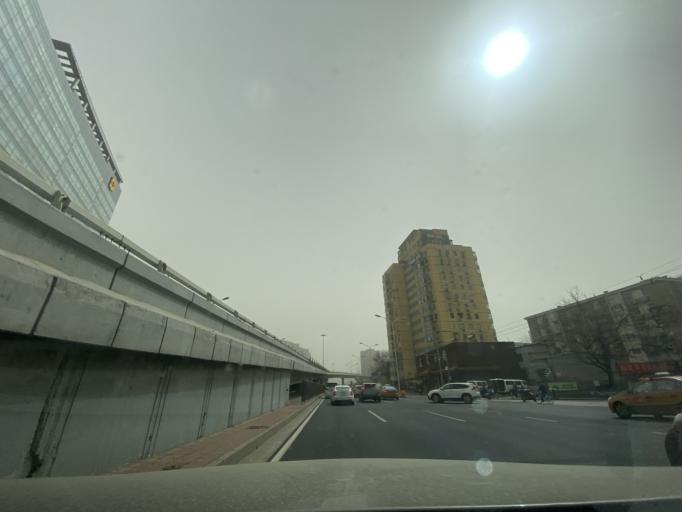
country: CN
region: Beijing
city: Sijiqing
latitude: 39.9423
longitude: 116.3003
